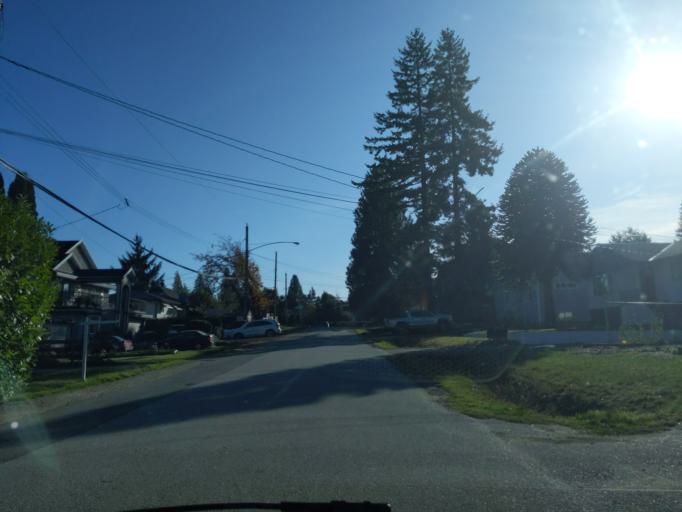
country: CA
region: British Columbia
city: New Westminster
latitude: 49.1999
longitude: -122.8607
